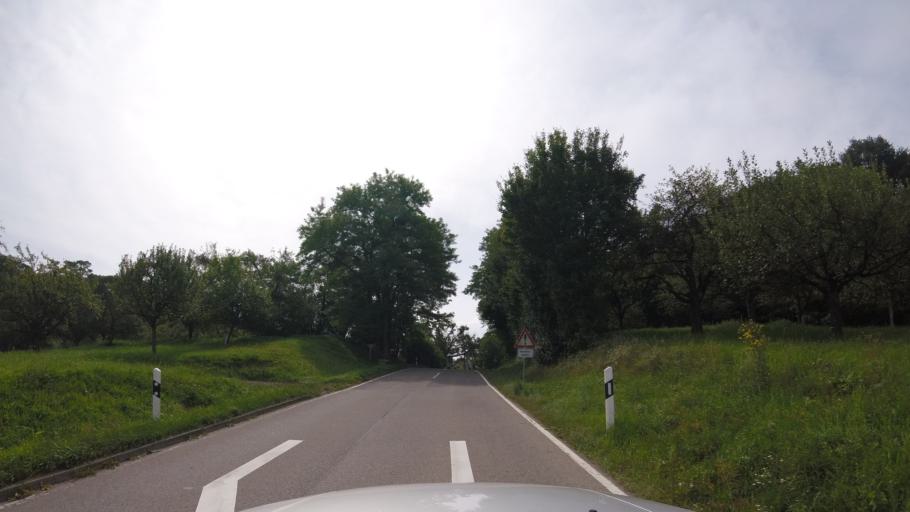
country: DE
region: Baden-Wuerttemberg
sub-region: Regierungsbezirk Stuttgart
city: Ilsfeld
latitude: 49.0307
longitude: 9.2697
